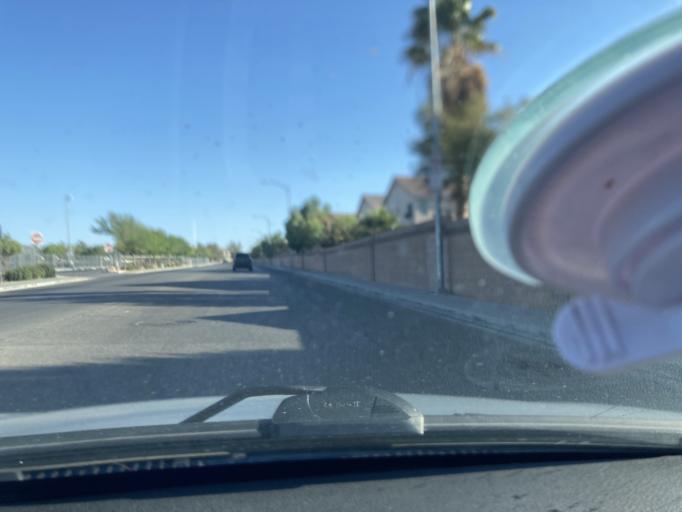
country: US
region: Nevada
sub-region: Clark County
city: Enterprise
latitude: 36.0625
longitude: -115.2930
